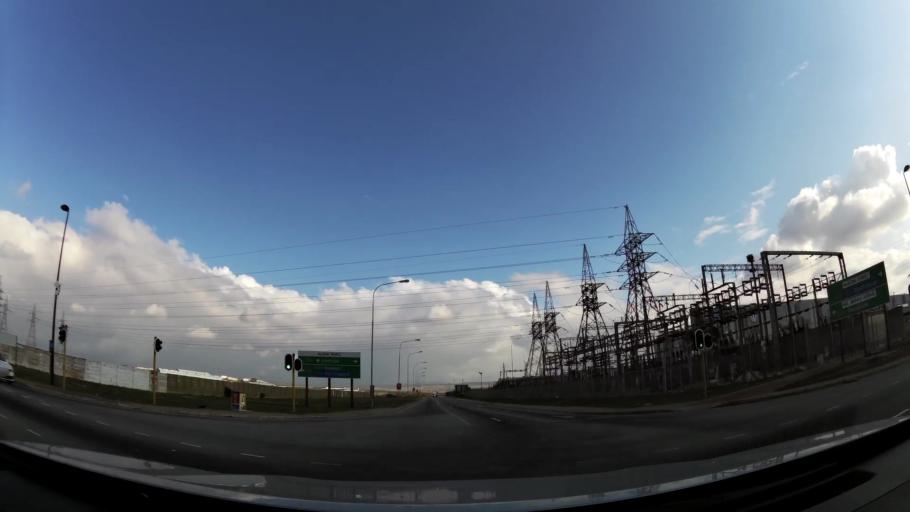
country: ZA
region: Eastern Cape
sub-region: Nelson Mandela Bay Metropolitan Municipality
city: Uitenhage
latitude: -33.7864
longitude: 25.4245
